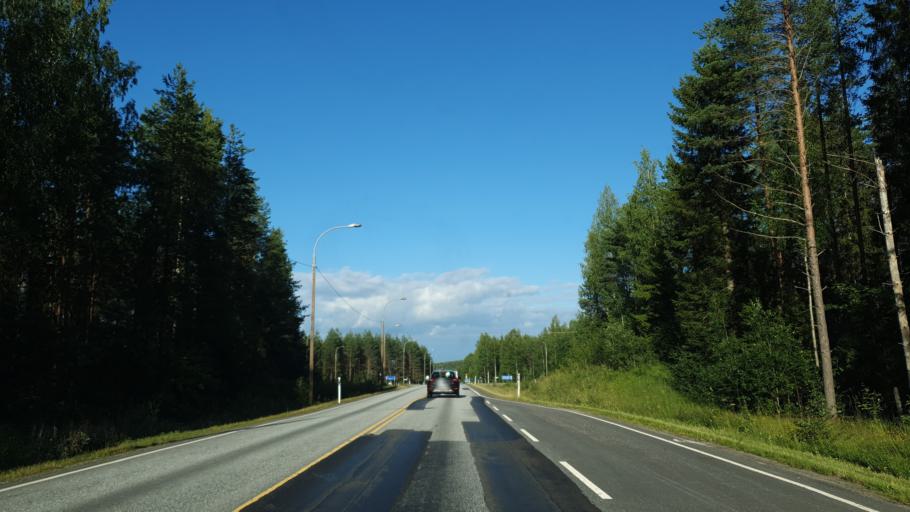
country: FI
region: North Karelia
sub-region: Joensuu
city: Outokumpu
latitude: 62.5217
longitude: 29.0386
